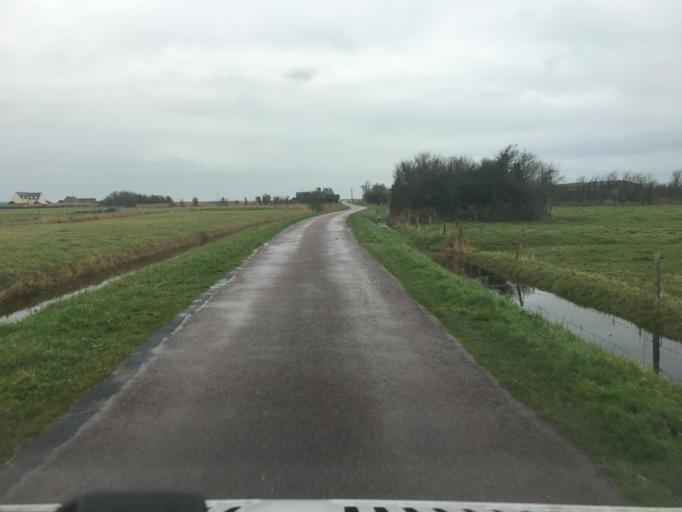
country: FR
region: Lower Normandy
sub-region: Departement de la Manche
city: Sainte-Mere-Eglise
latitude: 49.4509
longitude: -1.2260
